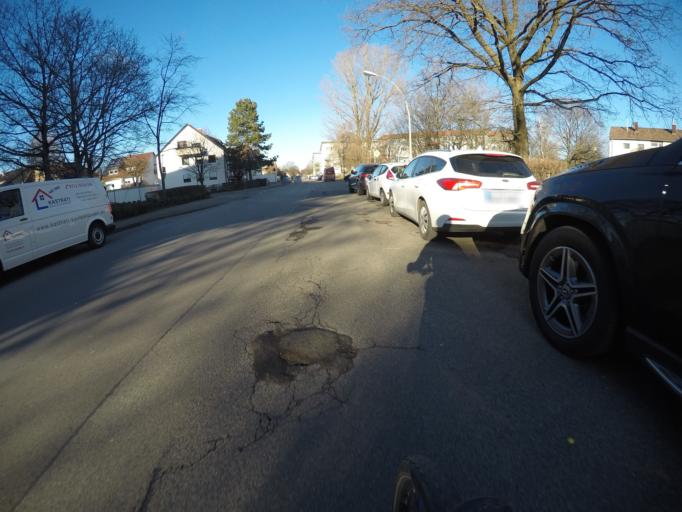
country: DE
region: Baden-Wuerttemberg
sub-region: Regierungsbezirk Stuttgart
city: Ostfildern
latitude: 48.7438
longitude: 9.2306
